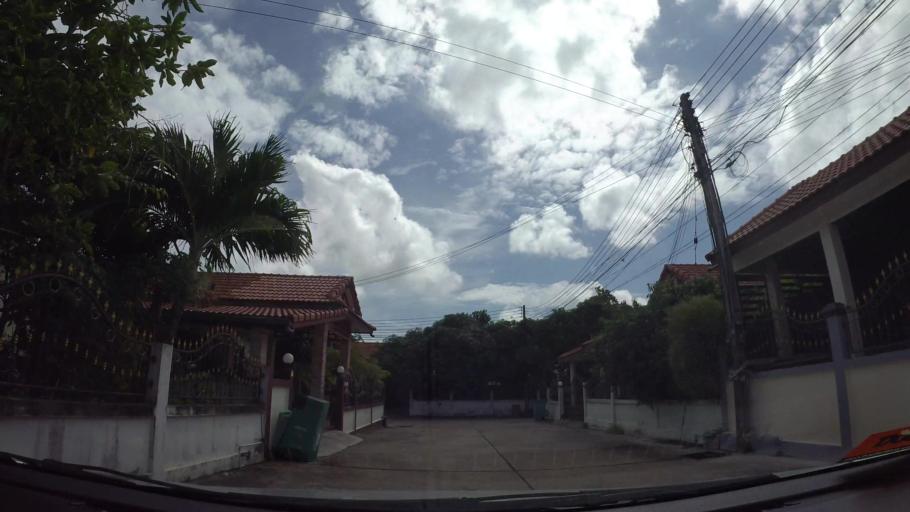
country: TH
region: Chon Buri
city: Sattahip
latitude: 12.6937
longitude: 100.9092
